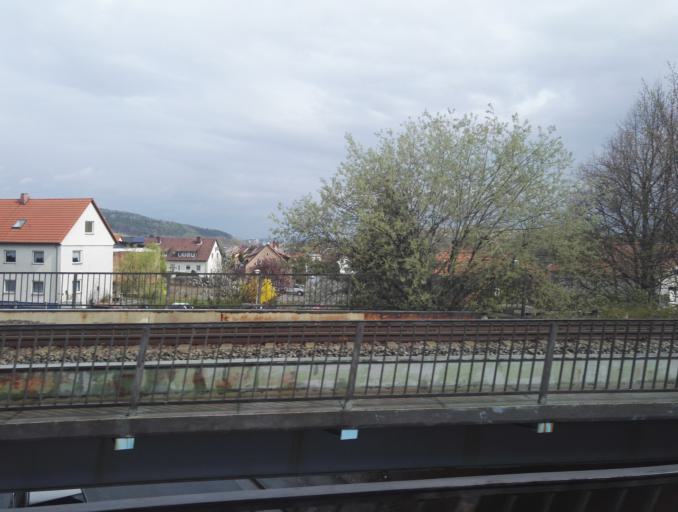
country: DE
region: Lower Saxony
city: Goslar
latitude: 51.9040
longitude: 10.4808
